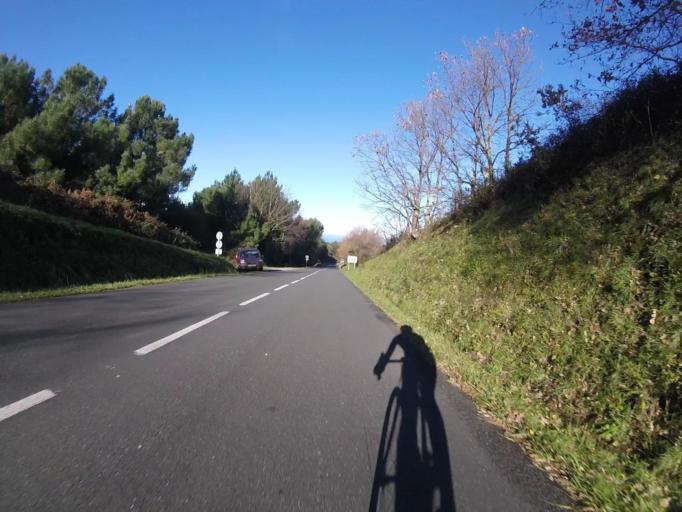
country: ES
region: Basque Country
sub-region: Provincia de Guipuzcoa
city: Fuenterrabia
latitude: 43.3681
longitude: -1.8317
